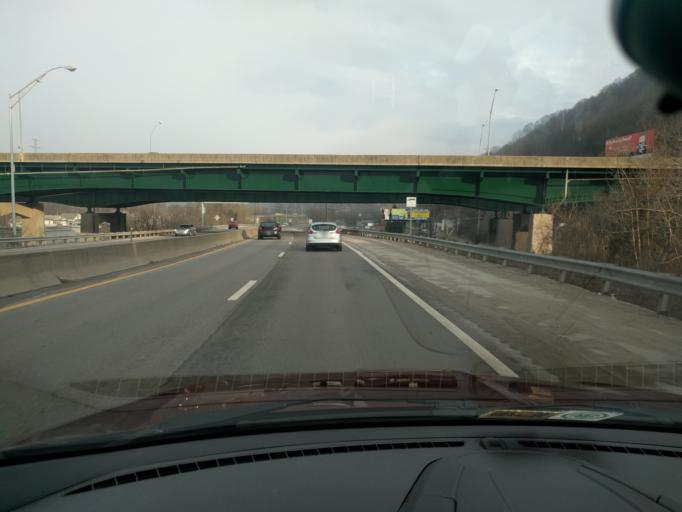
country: US
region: West Virginia
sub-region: Kanawha County
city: Rand
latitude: 38.3103
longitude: -81.5570
